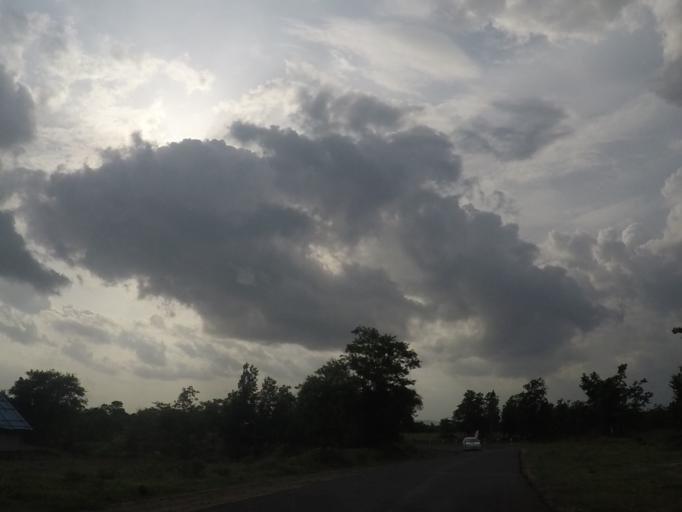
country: MM
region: Mandalay
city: Meiktila
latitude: 20.5240
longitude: 95.6483
